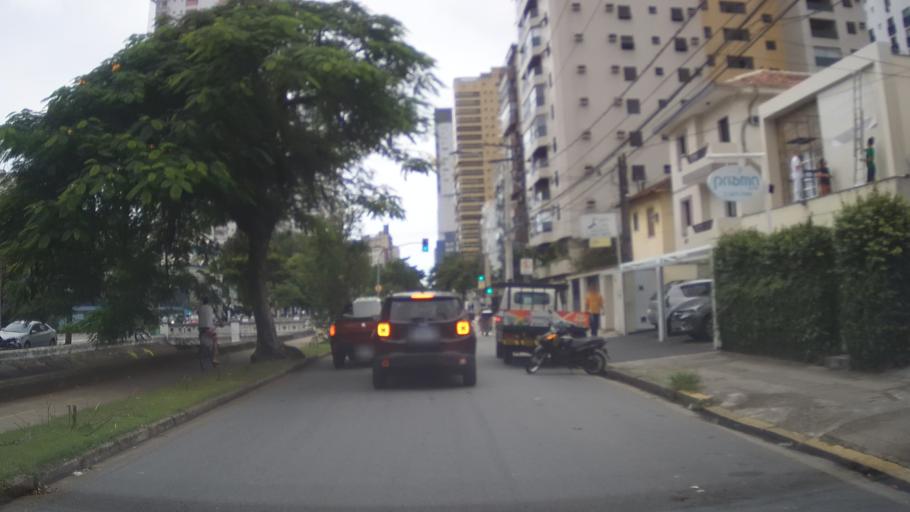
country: BR
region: Sao Paulo
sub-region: Santos
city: Santos
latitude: -23.9731
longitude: -46.3115
